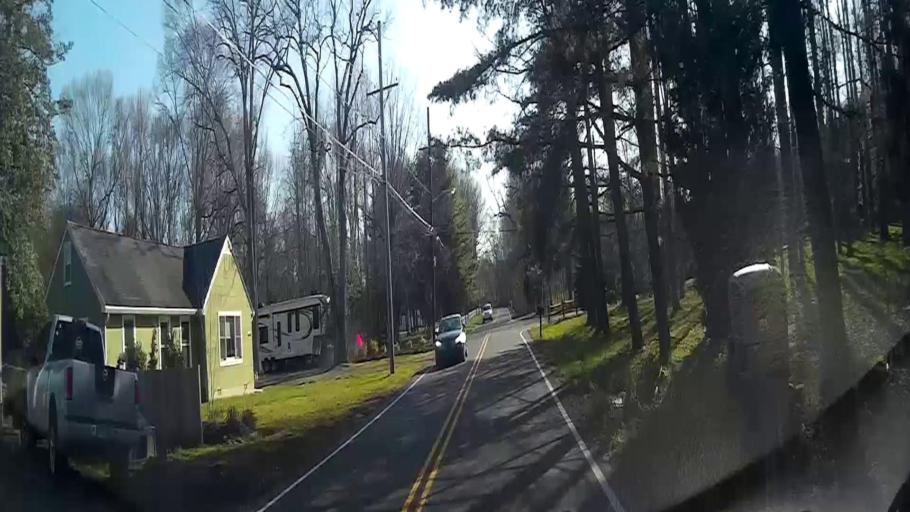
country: US
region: New Jersey
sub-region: Burlington County
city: Marlton
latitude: 39.8584
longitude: -74.9032
